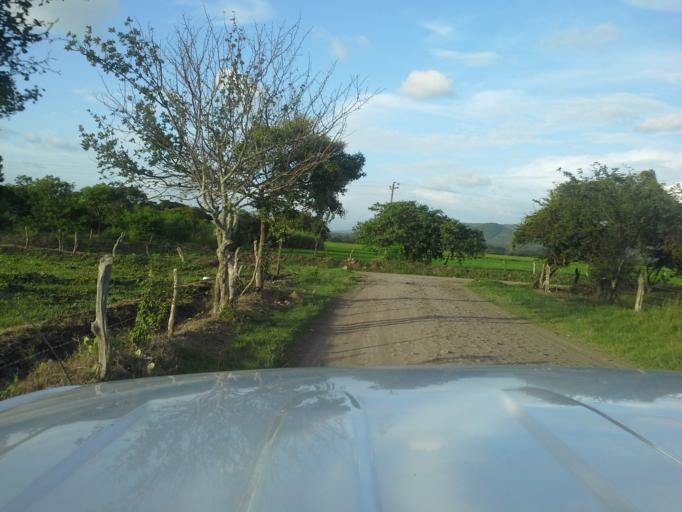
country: NI
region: Matagalpa
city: Ciudad Dario
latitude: 12.8034
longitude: -86.1387
